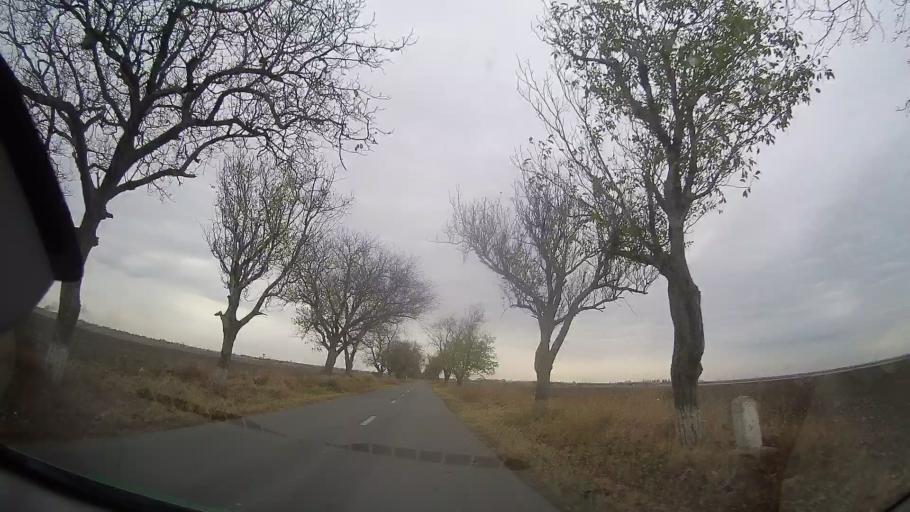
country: RO
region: Prahova
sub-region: Comuna Fantanele
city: Fantanele
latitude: 45.0122
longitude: 26.4117
